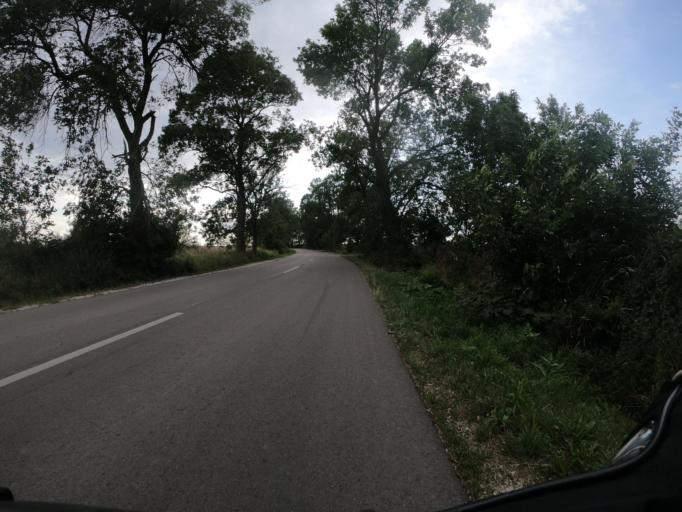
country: HU
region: Borsod-Abauj-Zemplen
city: Mezocsat
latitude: 47.8185
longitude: 20.8693
